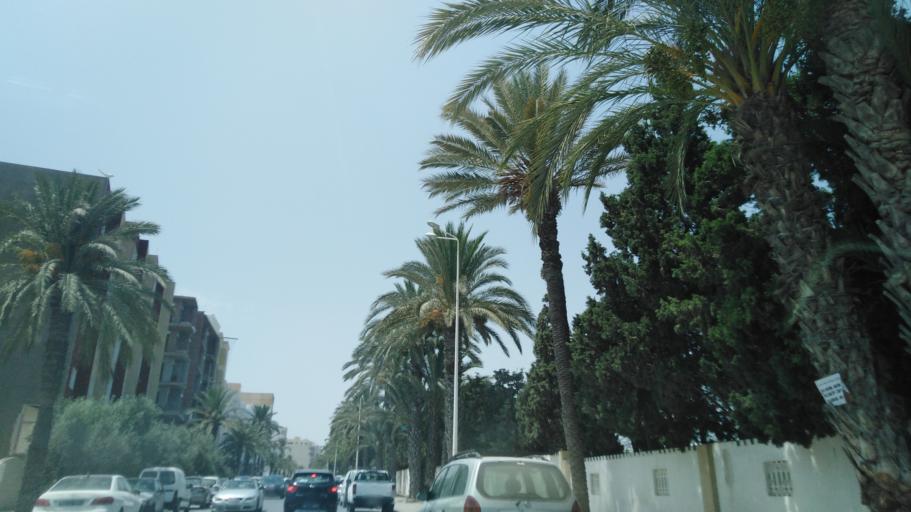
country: TN
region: Al Mahdiyah
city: Mahdia
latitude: 35.5238
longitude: 11.0384
